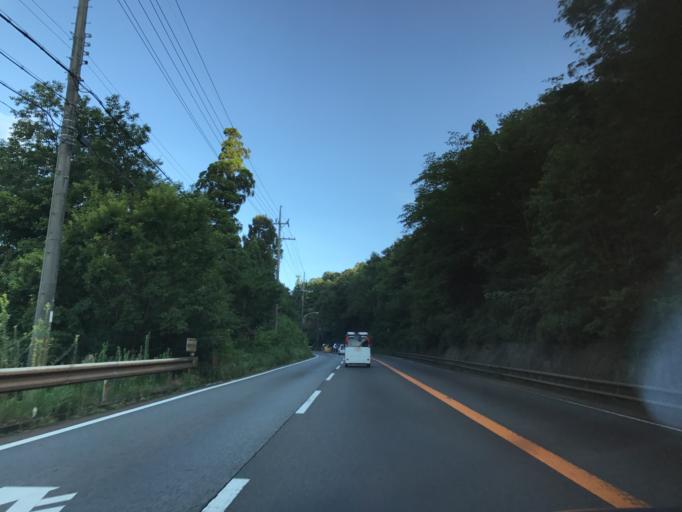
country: JP
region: Shiga Prefecture
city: Youkaichi
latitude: 35.0706
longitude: 136.2482
